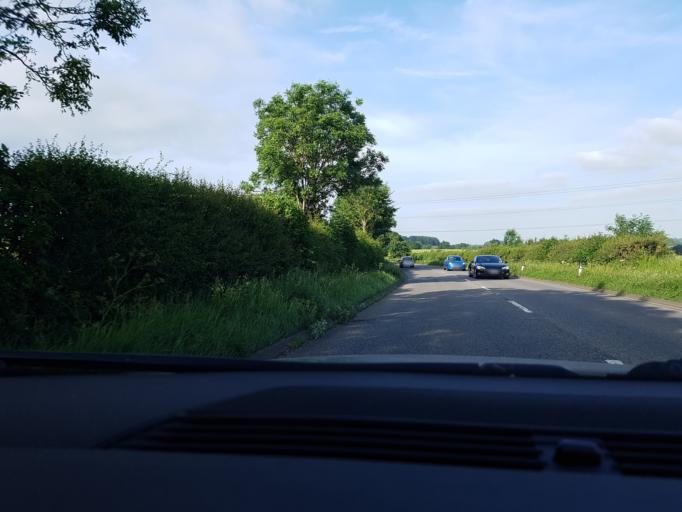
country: GB
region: England
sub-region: Buckinghamshire
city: Buckingham
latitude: 52.0076
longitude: -0.9542
